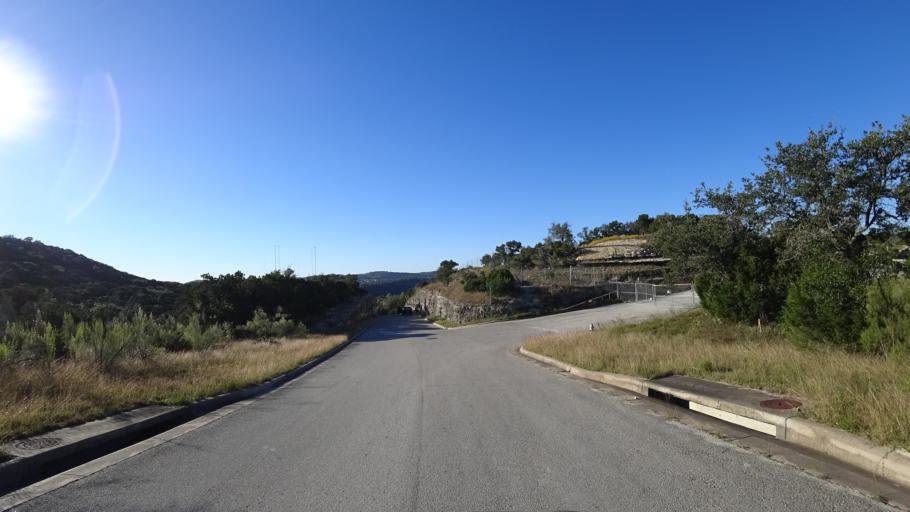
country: US
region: Texas
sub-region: Travis County
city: West Lake Hills
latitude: 30.3576
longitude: -97.8123
